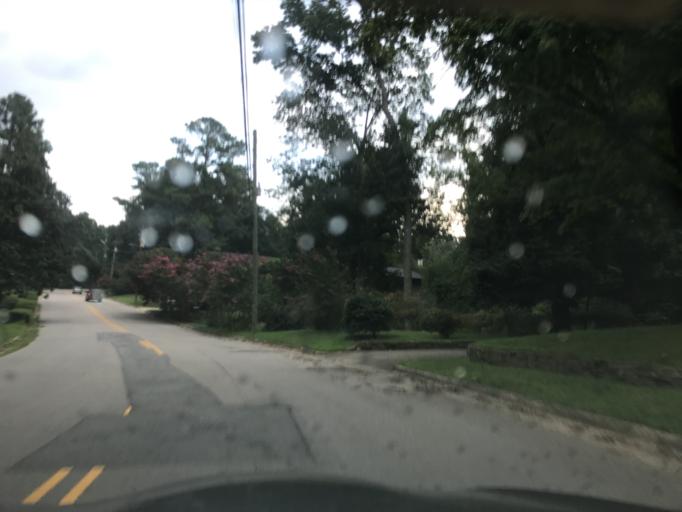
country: US
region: North Carolina
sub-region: Wake County
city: West Raleigh
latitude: 35.8097
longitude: -78.6623
